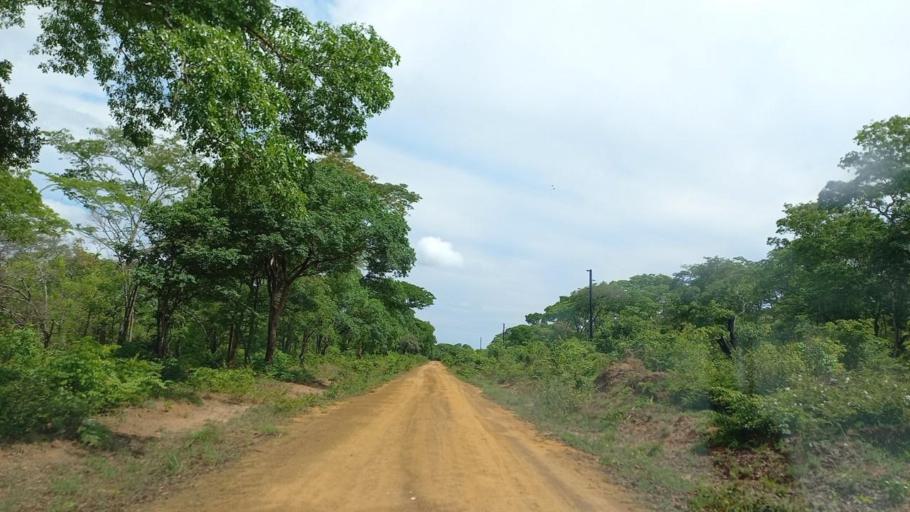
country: ZM
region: North-Western
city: Kabompo
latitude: -13.5361
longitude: 24.0968
